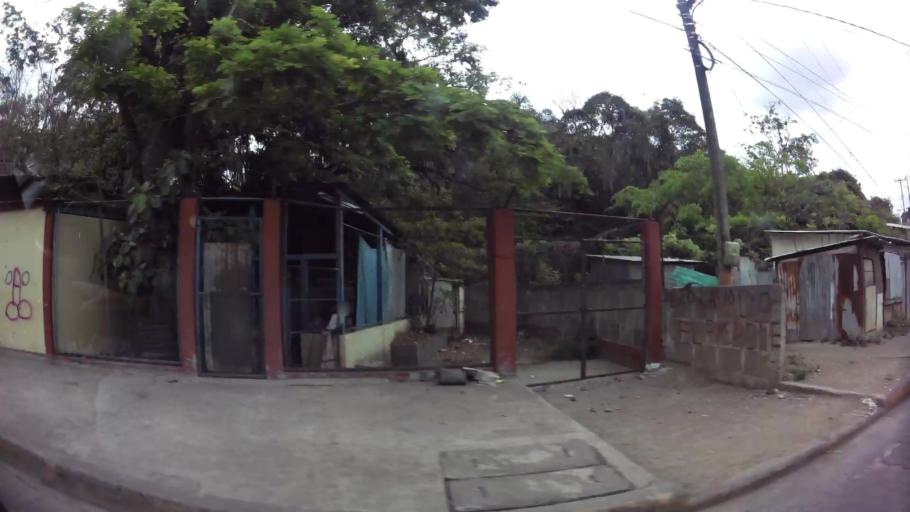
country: NI
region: Matagalpa
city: Matagalpa
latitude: 12.9363
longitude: -85.9102
